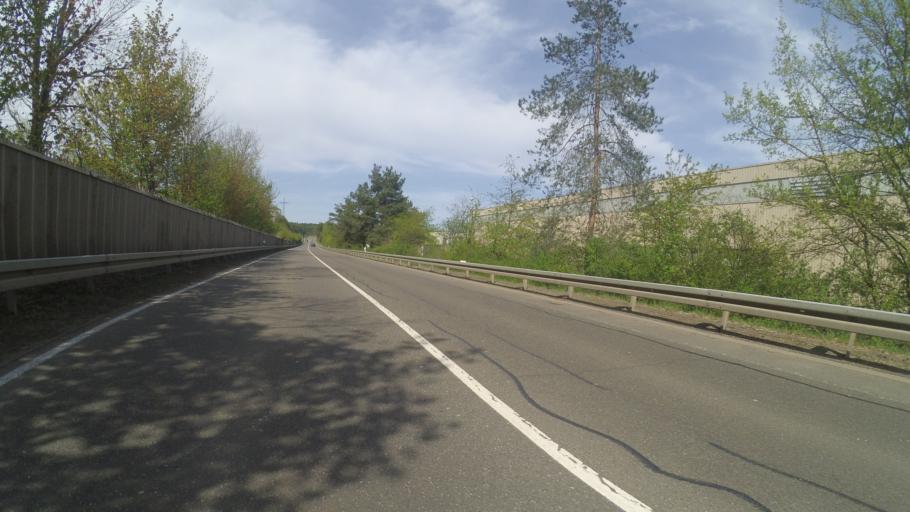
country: DE
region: Saarland
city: Homburg
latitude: 49.3413
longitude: 7.3418
